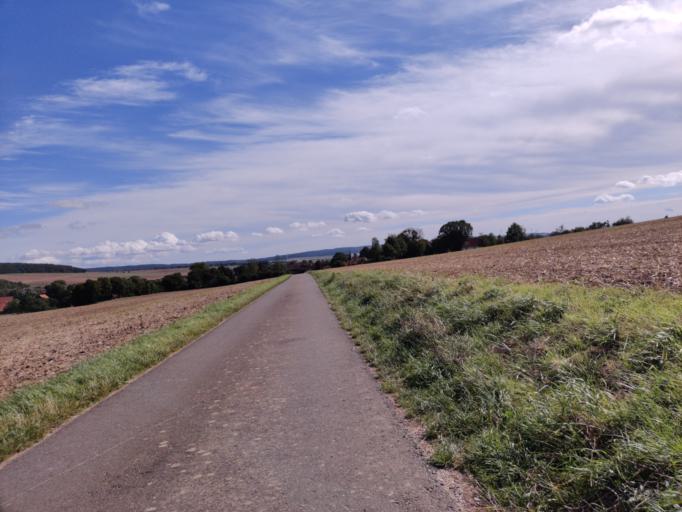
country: DE
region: Lower Saxony
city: Baddeckenstedt
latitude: 52.0834
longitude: 10.2222
